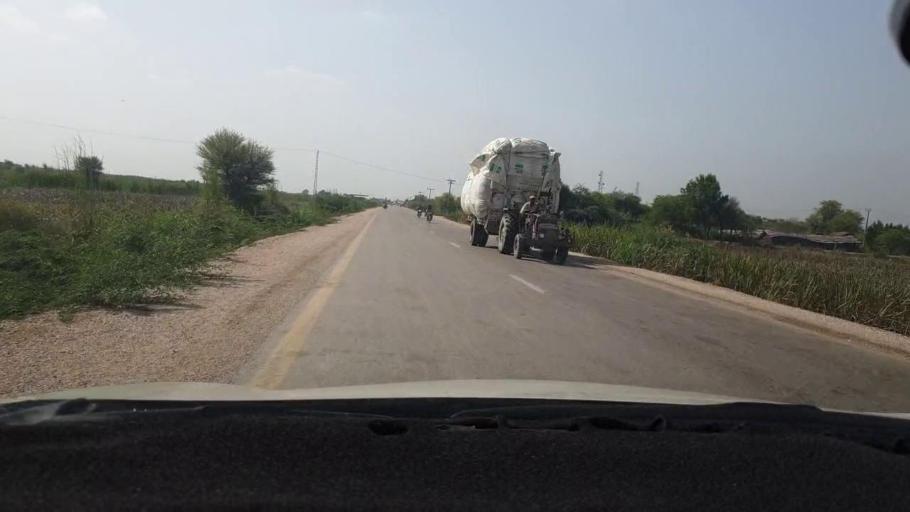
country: PK
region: Sindh
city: Tando Mittha Khan
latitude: 25.8071
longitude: 69.0724
